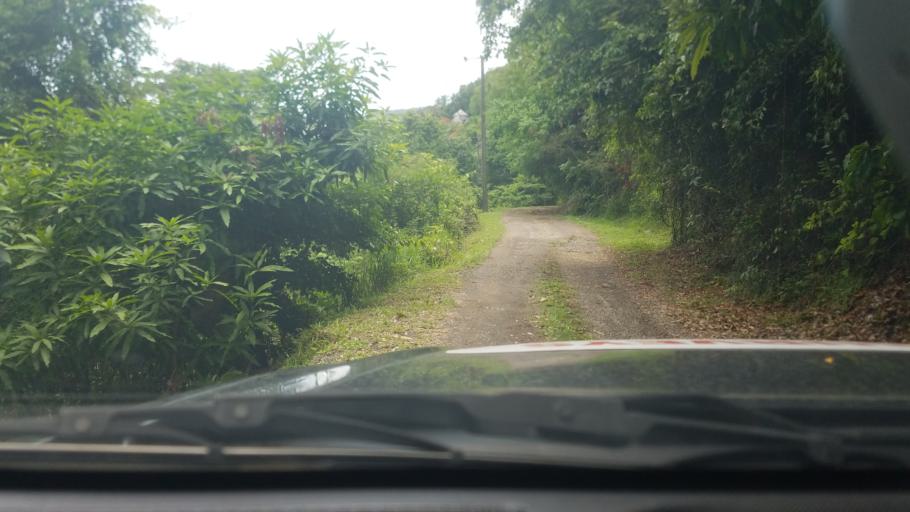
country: LC
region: Soufriere
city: Soufriere
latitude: 13.8428
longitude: -61.0626
